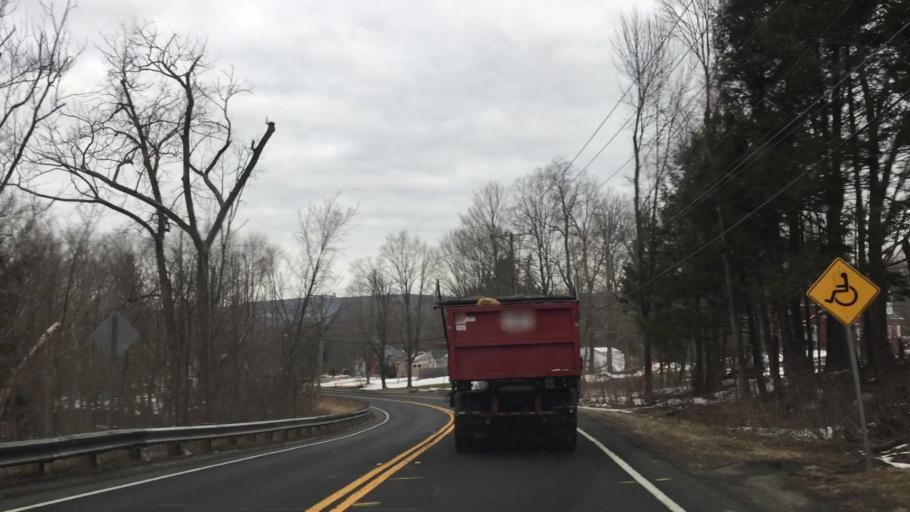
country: US
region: Massachusetts
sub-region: Berkshire County
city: Hinsdale
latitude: 42.4637
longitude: -73.1376
